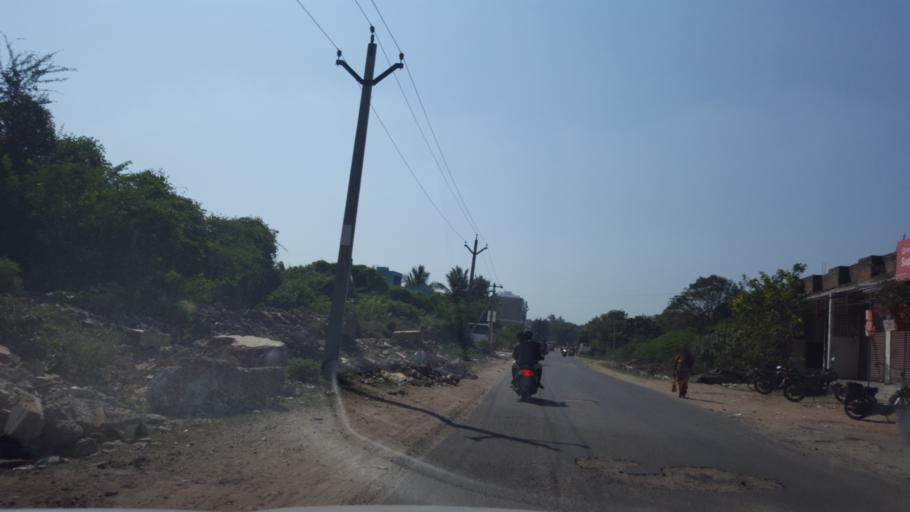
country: IN
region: Tamil Nadu
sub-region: Kancheepuram
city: Kanchipuram
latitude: 12.8391
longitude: 79.7167
